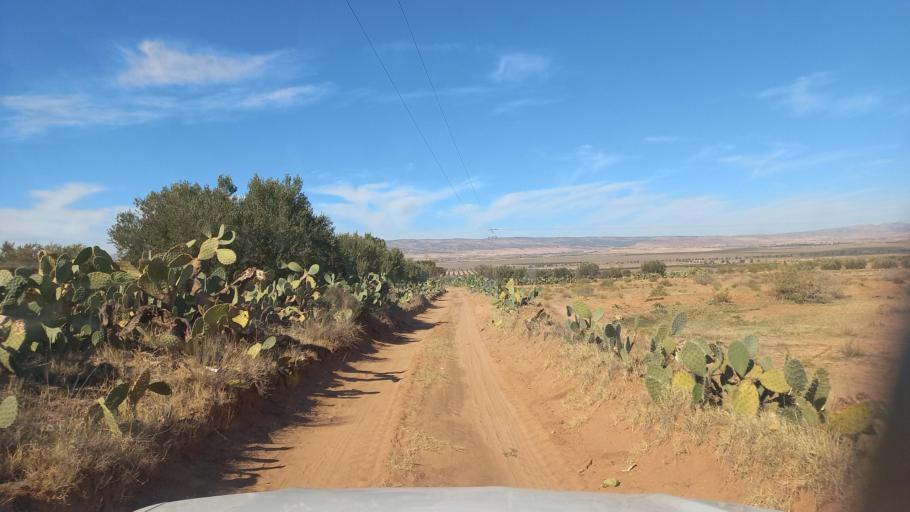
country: TN
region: Al Qasrayn
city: Kasserine
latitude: 35.2044
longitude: 8.9703
